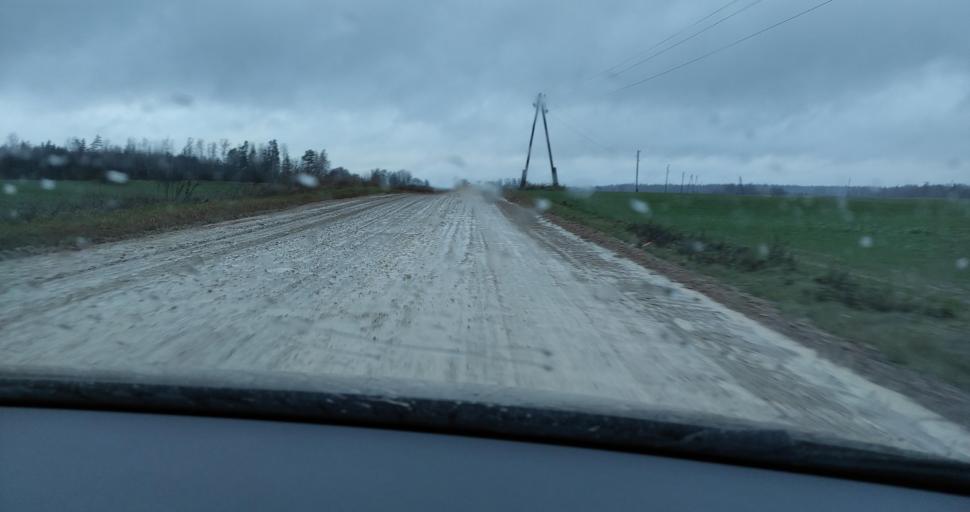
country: LV
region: Skrunda
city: Skrunda
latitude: 56.6913
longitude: 22.2208
